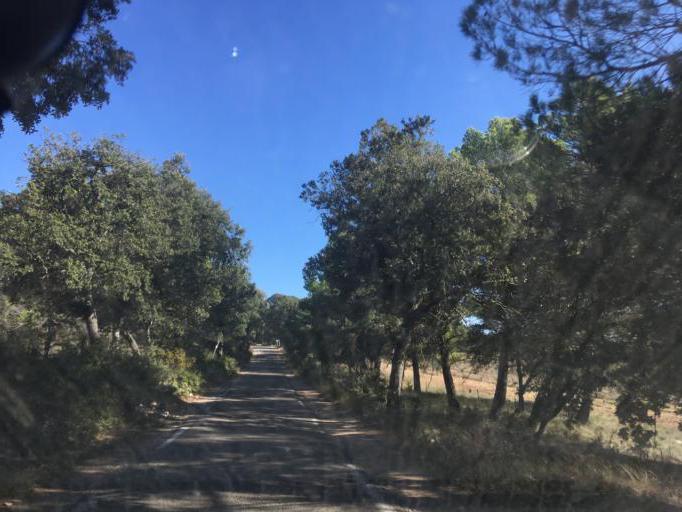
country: FR
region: Provence-Alpes-Cote d'Azur
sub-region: Departement du Var
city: Regusse
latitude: 43.7314
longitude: 6.1108
